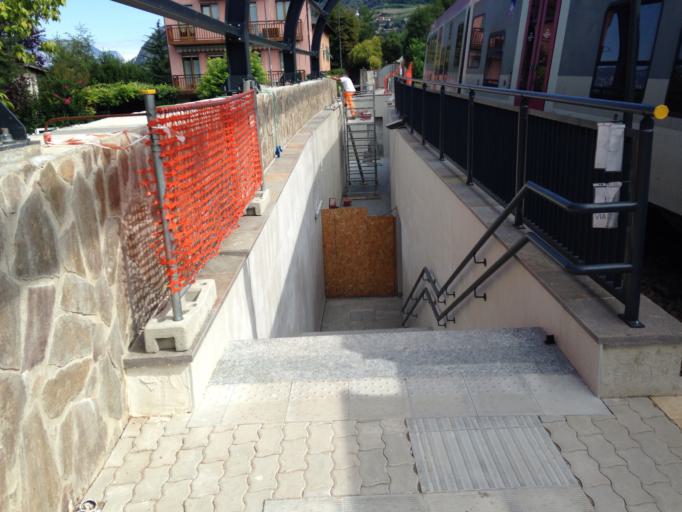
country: IT
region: Trentino-Alto Adige
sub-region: Provincia di Trento
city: Povo
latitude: 46.0659
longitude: 11.1425
